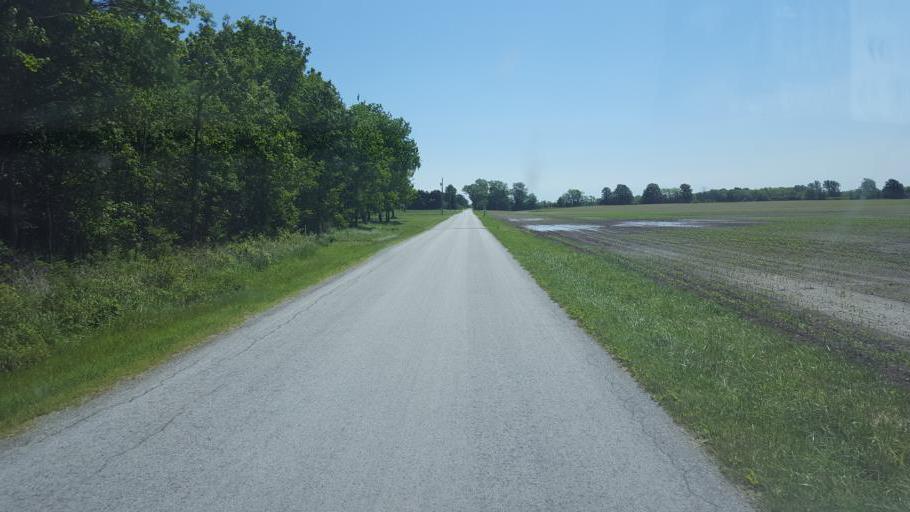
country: US
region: Ohio
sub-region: Hardin County
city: Forest
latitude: 40.6512
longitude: -83.4360
